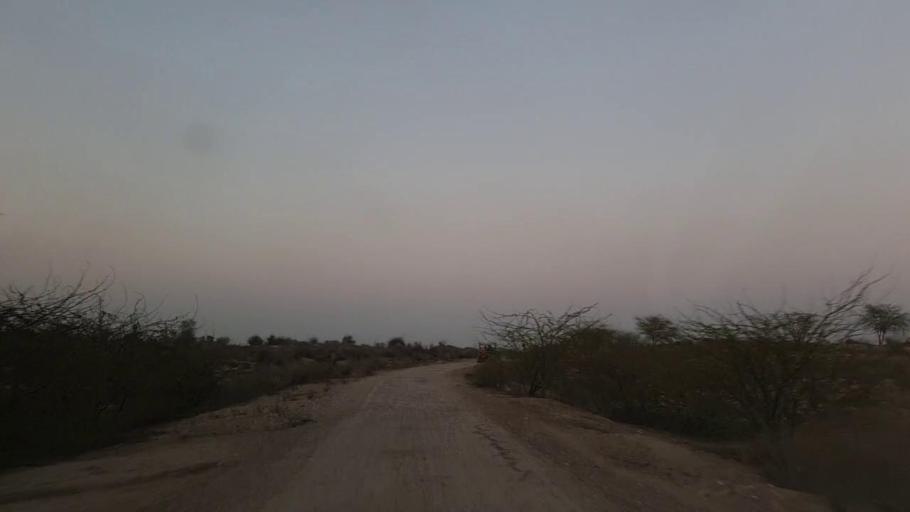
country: PK
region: Sindh
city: Bandhi
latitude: 26.6068
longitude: 68.3791
